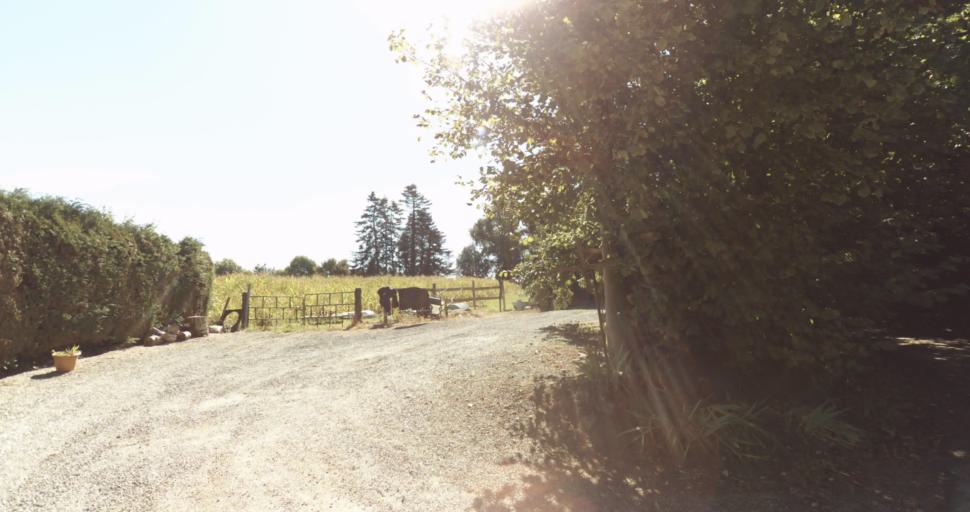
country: FR
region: Lower Normandy
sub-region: Departement de l'Orne
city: Gace
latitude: 48.7845
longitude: 0.2744
